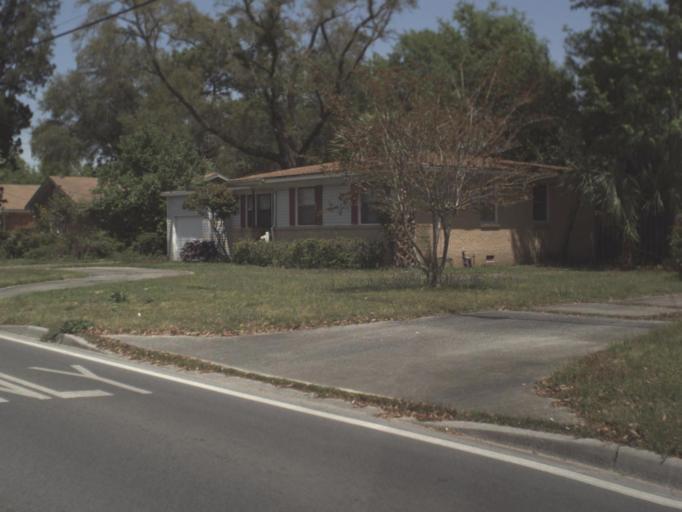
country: US
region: Florida
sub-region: Escambia County
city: Goulding
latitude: 30.4648
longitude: -87.2035
